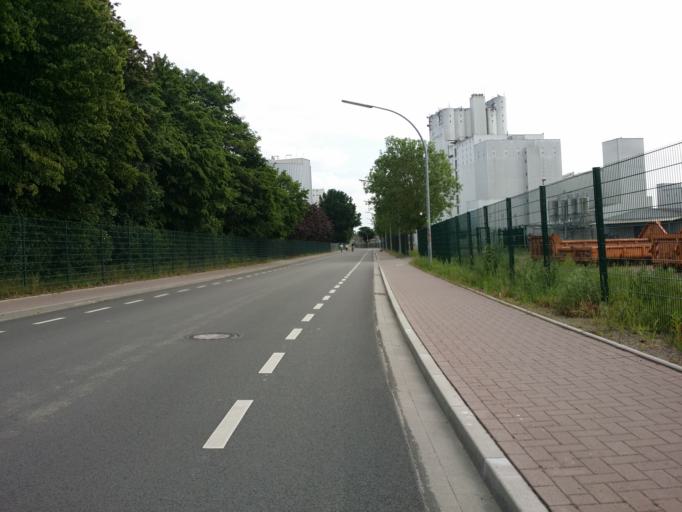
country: DE
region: Lower Saxony
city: Oldenburg
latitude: 53.1451
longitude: 8.2434
